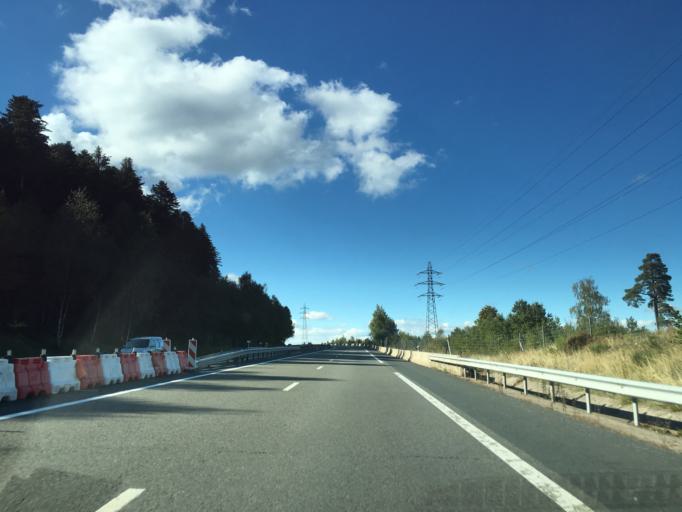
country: FR
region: Lorraine
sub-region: Departement des Vosges
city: Etival-Clairefontaine
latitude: 48.3955
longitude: 6.8475
